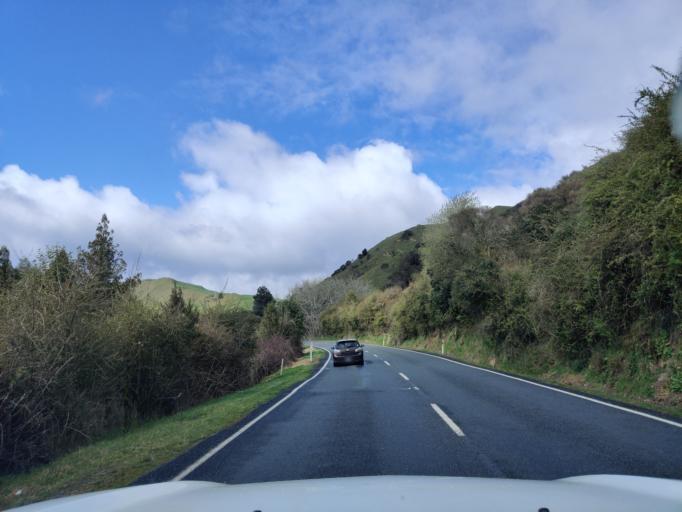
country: NZ
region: Waikato
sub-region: Otorohanga District
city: Otorohanga
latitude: -38.5900
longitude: 175.2177
